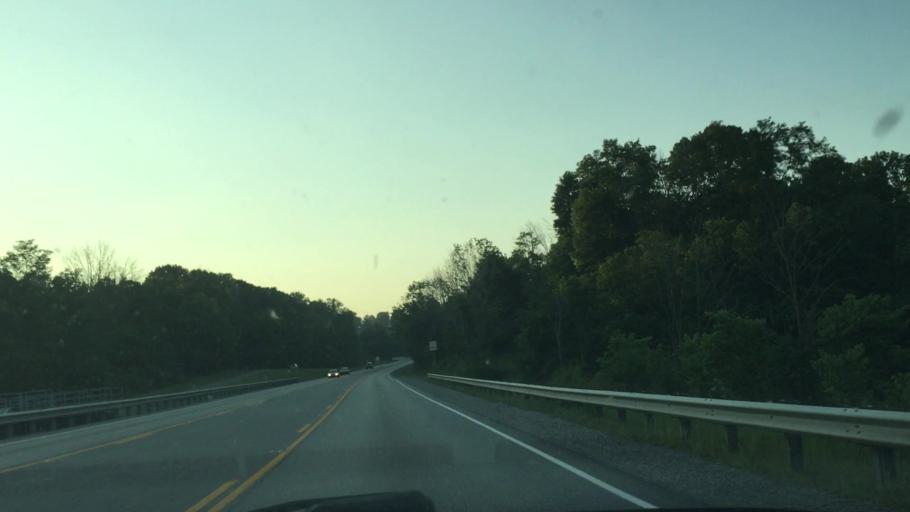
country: US
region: Kentucky
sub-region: Carroll County
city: Carrollton
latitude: 38.6699
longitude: -85.1460
